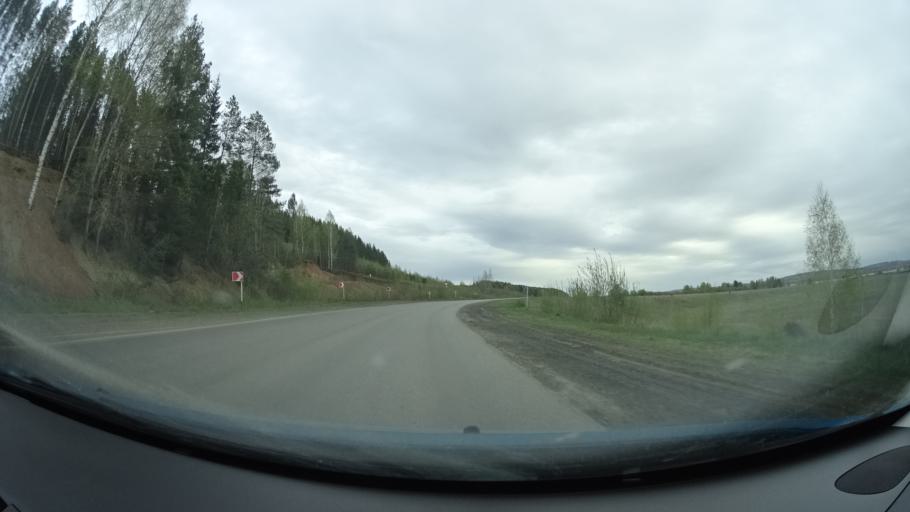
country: RU
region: Perm
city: Osa
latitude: 57.2186
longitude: 55.5921
